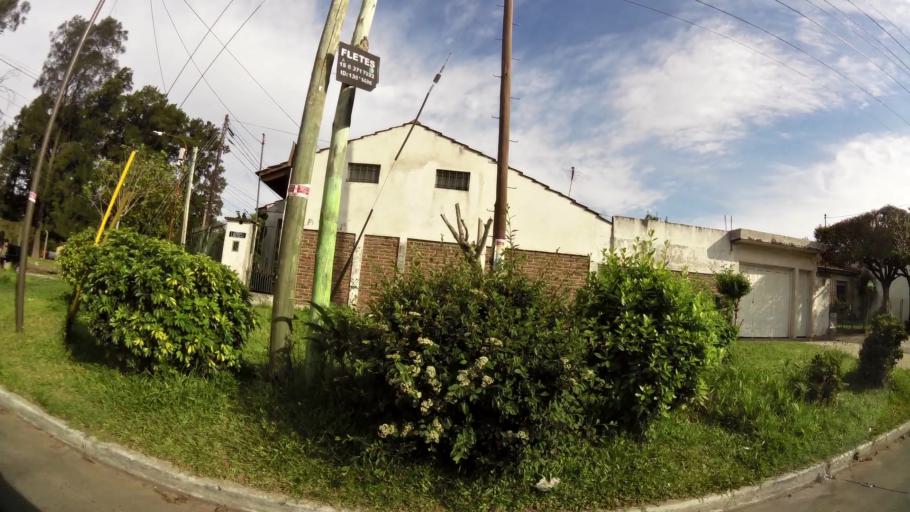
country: AR
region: Buenos Aires
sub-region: Partido de Quilmes
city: Quilmes
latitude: -34.7500
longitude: -58.2749
